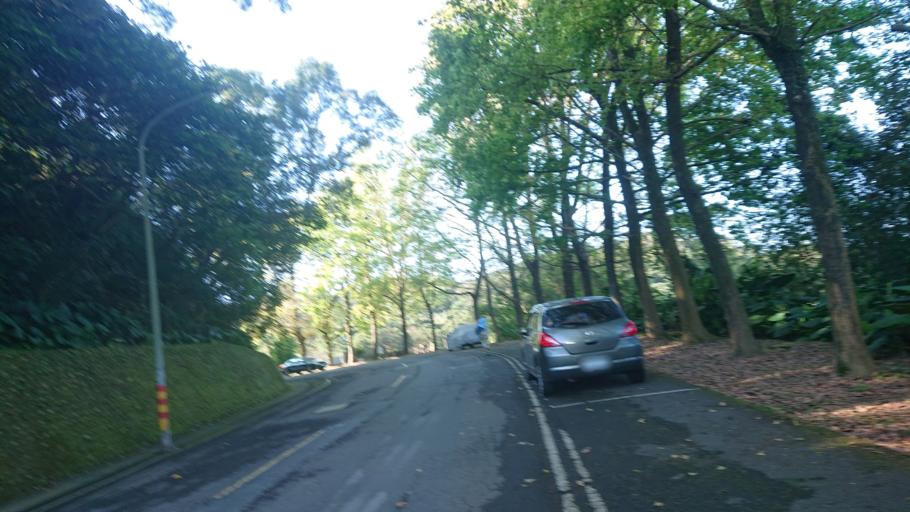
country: TW
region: Taipei
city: Taipei
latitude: 24.9794
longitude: 121.5690
